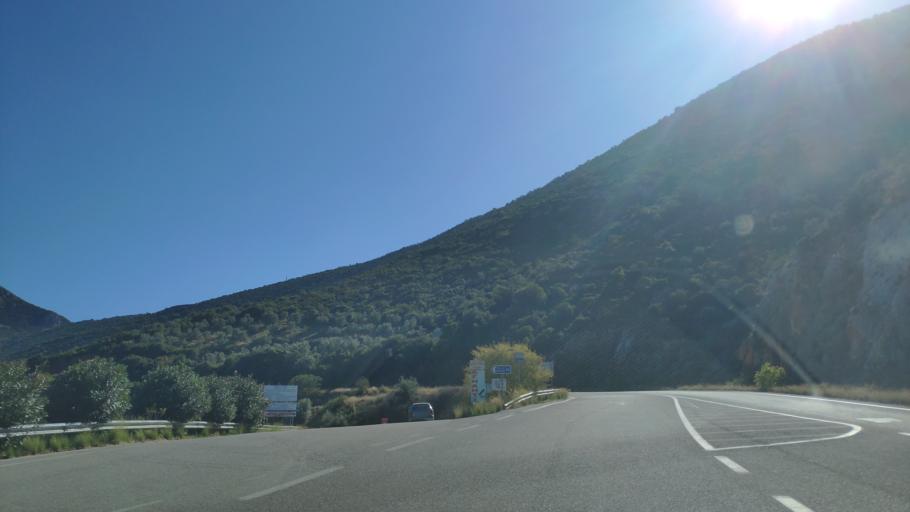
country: GR
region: Peloponnese
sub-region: Nomos Argolidos
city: Palaia Epidavros
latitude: 37.6120
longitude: 23.1521
